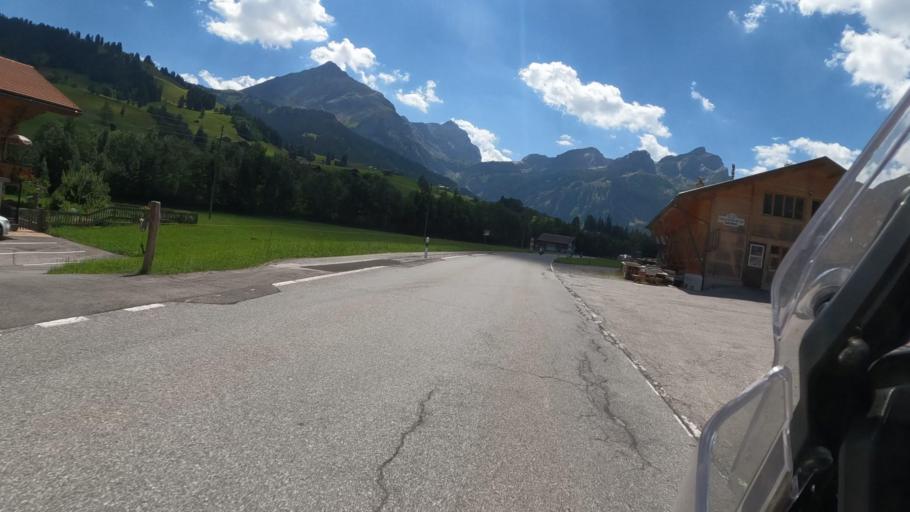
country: CH
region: Bern
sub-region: Obersimmental-Saanen District
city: Gstaad
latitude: 46.4060
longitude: 7.2683
